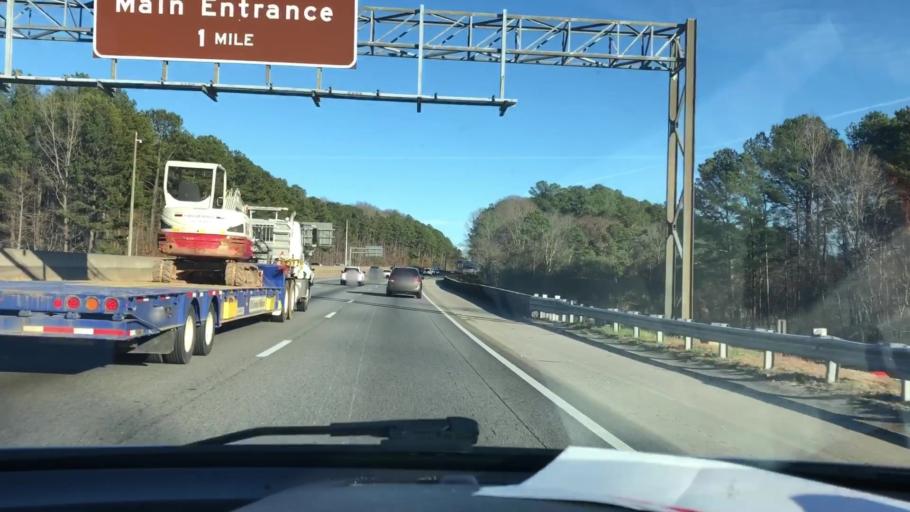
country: US
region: Georgia
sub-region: DeKalb County
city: Stone Mountain
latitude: 33.8238
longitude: -84.1534
